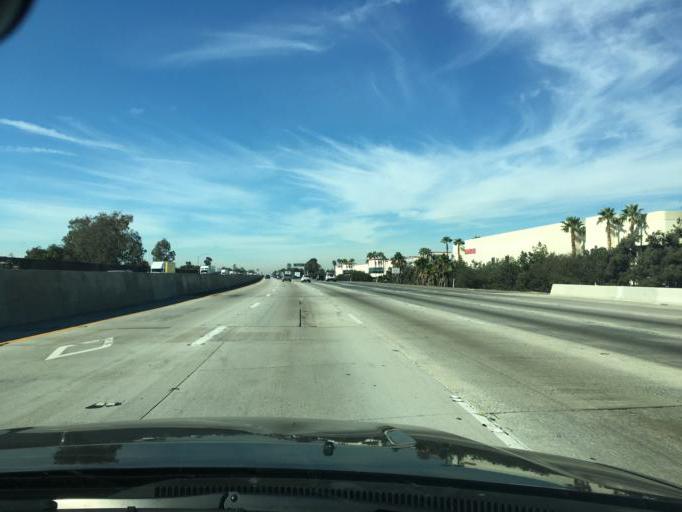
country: US
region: California
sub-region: San Bernardino County
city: Ontario
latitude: 34.0306
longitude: -117.5839
